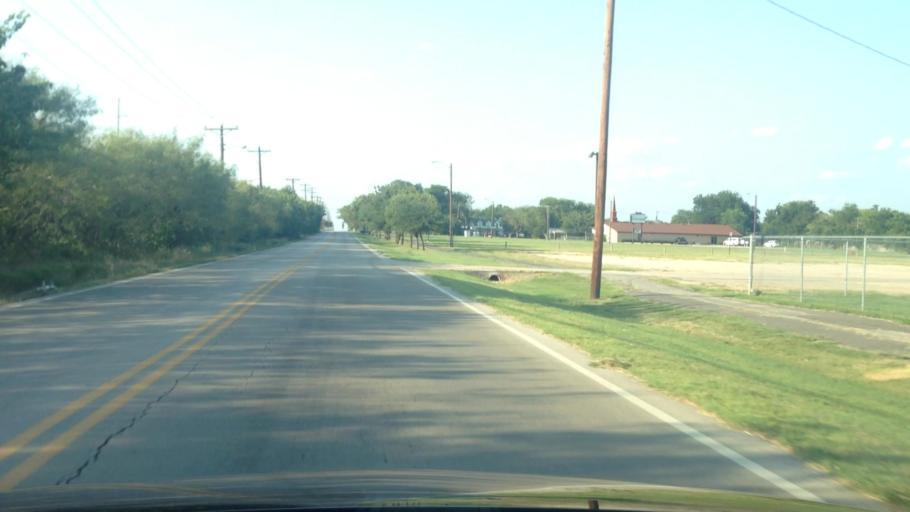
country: US
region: Texas
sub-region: Tarrant County
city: Everman
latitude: 32.6358
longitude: -97.2882
